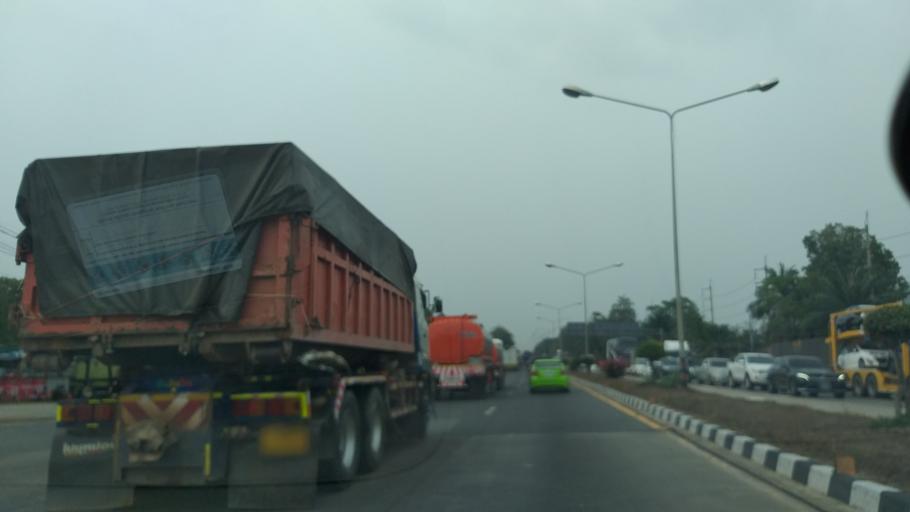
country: TH
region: Chon Buri
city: Ko Chan
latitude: 13.3254
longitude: 101.2702
